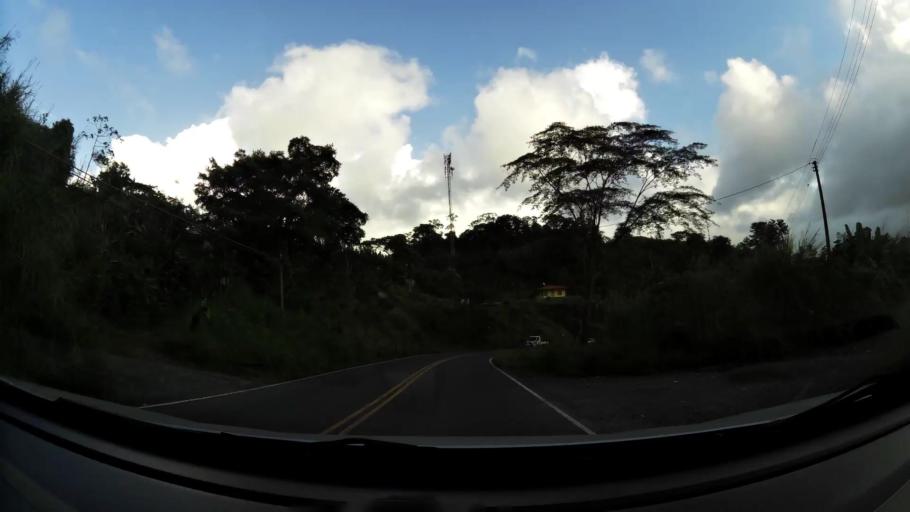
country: CR
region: Limon
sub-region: Canton de Siquirres
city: Siquirres
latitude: 10.0003
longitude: -83.5739
